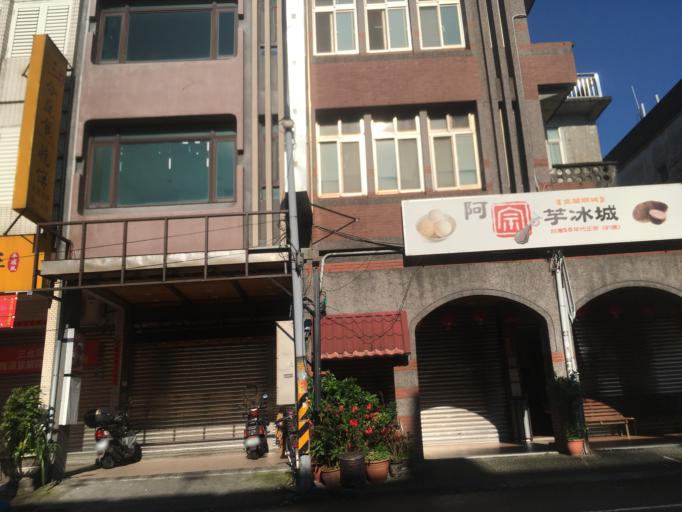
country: TW
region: Taiwan
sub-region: Yilan
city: Yilan
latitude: 24.8587
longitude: 121.8261
